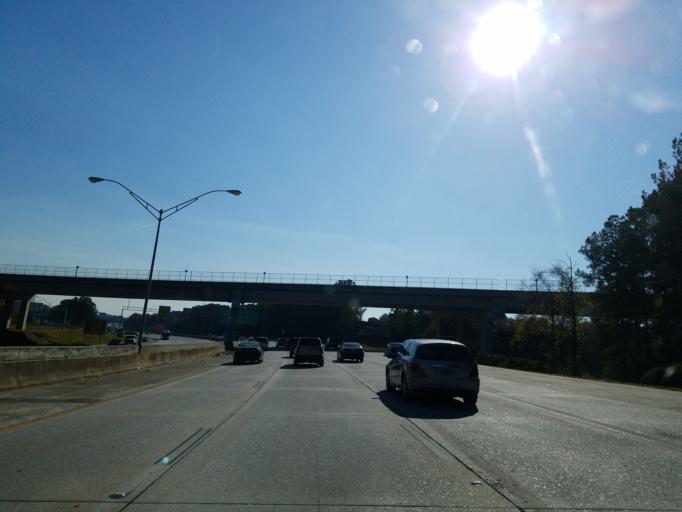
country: US
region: Georgia
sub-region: Fulton County
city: College Park
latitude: 33.6372
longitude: -84.4569
